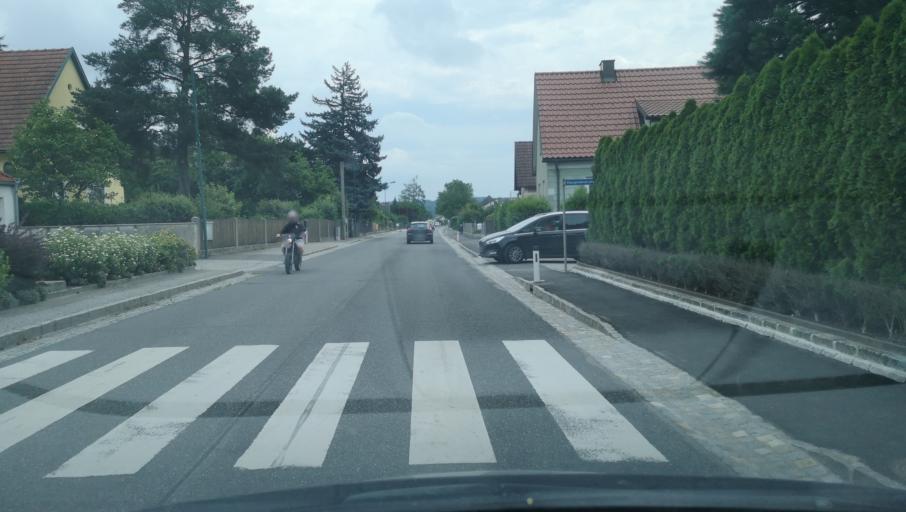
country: AT
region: Lower Austria
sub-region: Politischer Bezirk Melk
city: Ybbs an der Donau
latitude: 48.1882
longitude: 15.0877
